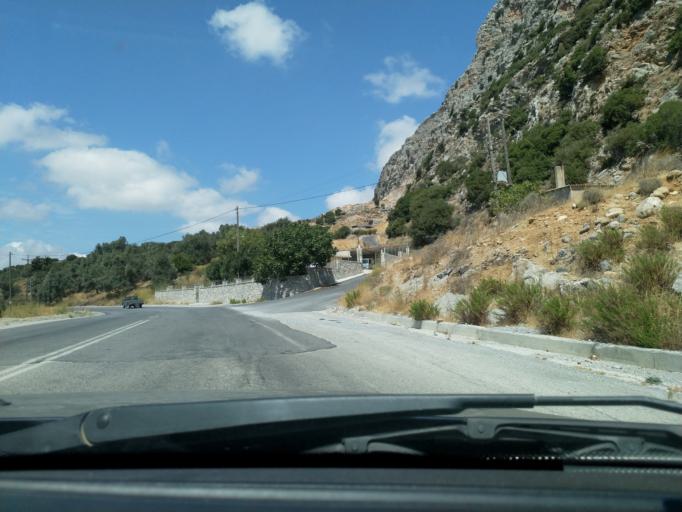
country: GR
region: Crete
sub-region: Nomos Rethymnis
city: Agia Foteini
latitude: 35.2065
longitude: 24.5409
